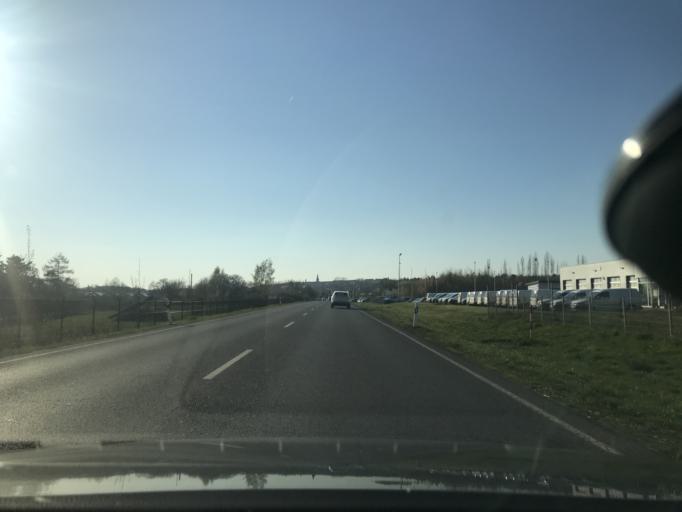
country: DE
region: Thuringia
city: Nordhausen
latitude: 51.4910
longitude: 10.8264
